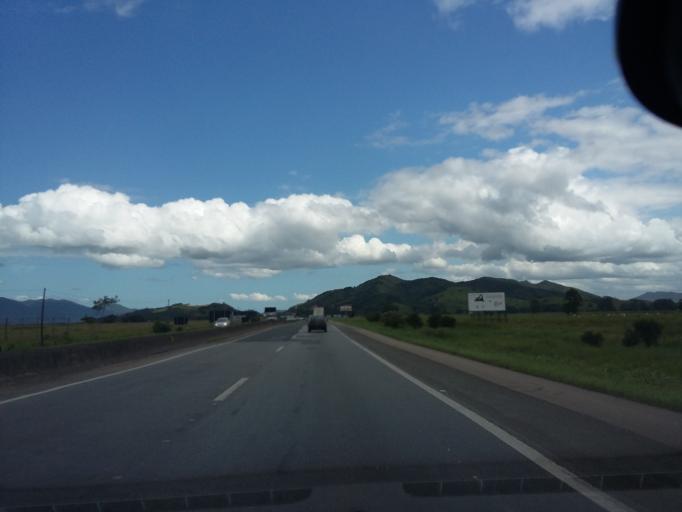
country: BR
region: Santa Catarina
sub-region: Tijucas
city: Tijucas
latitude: -27.2558
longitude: -48.6315
